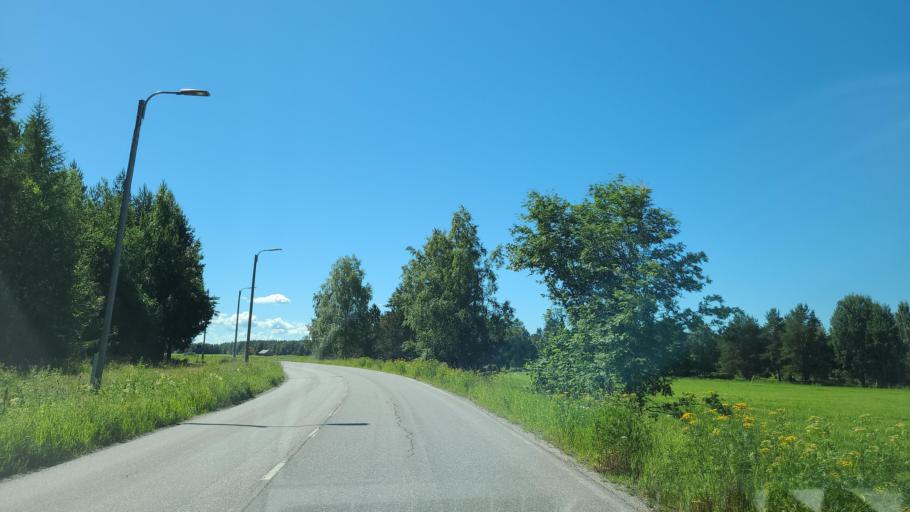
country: FI
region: Ostrobothnia
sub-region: Vaasa
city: Ristinummi
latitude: 63.0682
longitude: 21.7240
